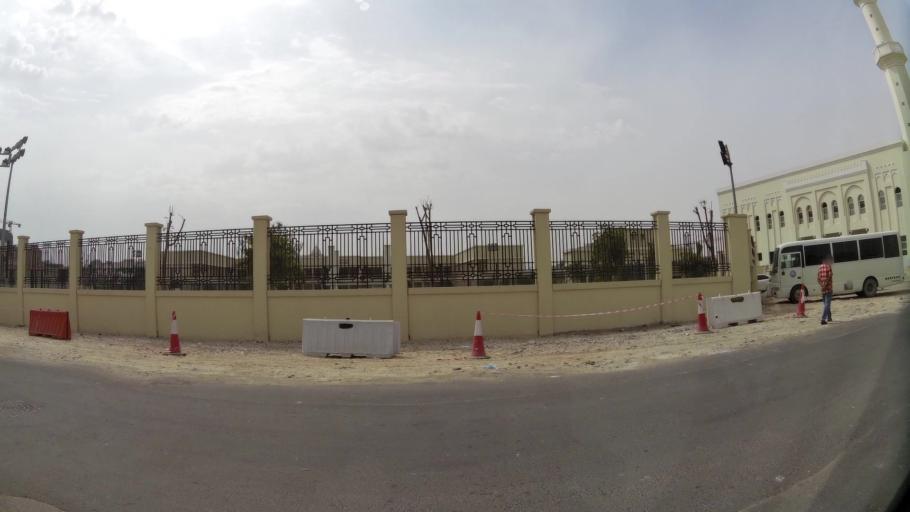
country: QA
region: Baladiyat ad Dawhah
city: Doha
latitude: 25.2846
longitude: 51.4988
